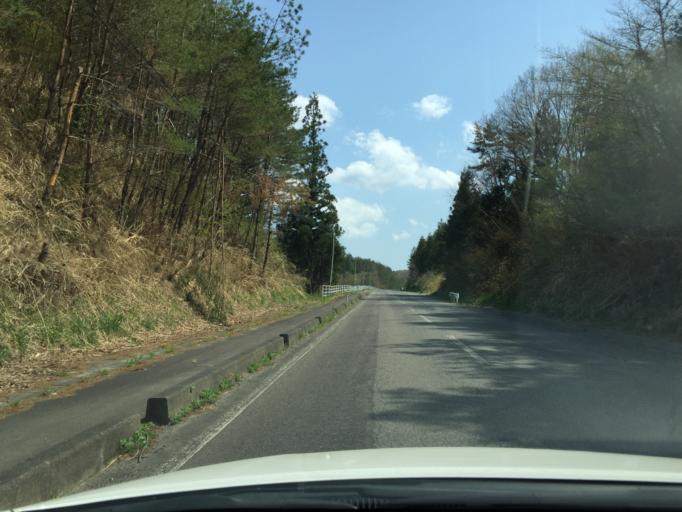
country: JP
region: Fukushima
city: Namie
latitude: 37.4059
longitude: 140.7975
